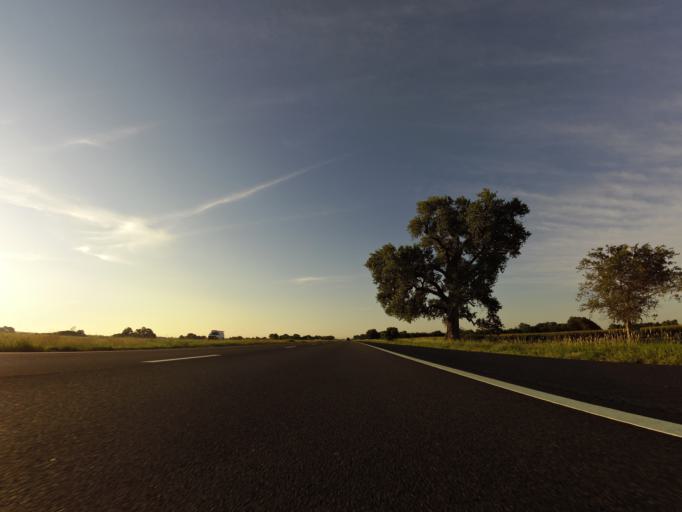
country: US
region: Kansas
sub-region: Sedgwick County
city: Colwich
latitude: 37.8188
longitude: -97.5097
